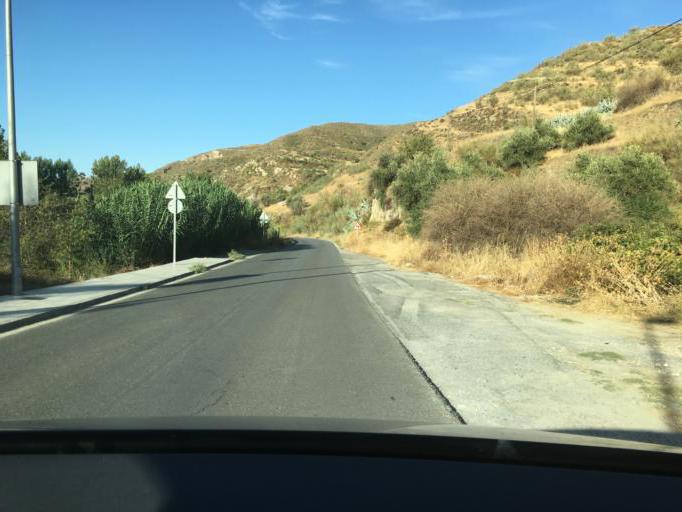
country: ES
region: Andalusia
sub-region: Provincia de Granada
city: Dudar
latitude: 37.1857
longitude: -3.4872
